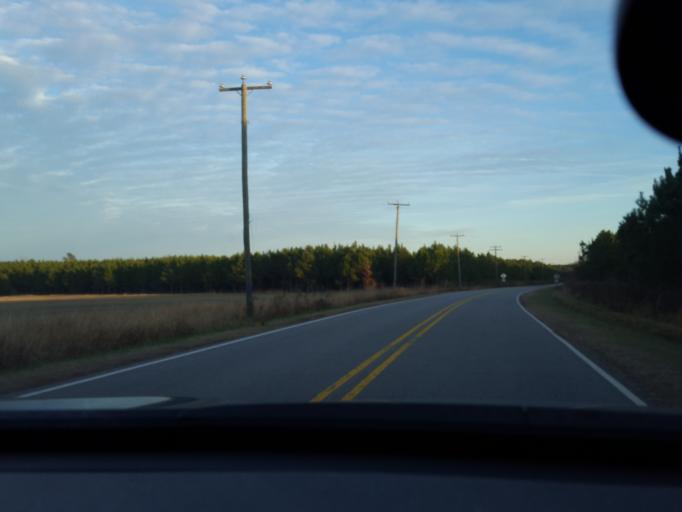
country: US
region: North Carolina
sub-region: Hertford County
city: Ahoskie
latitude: 36.2756
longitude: -77.1551
